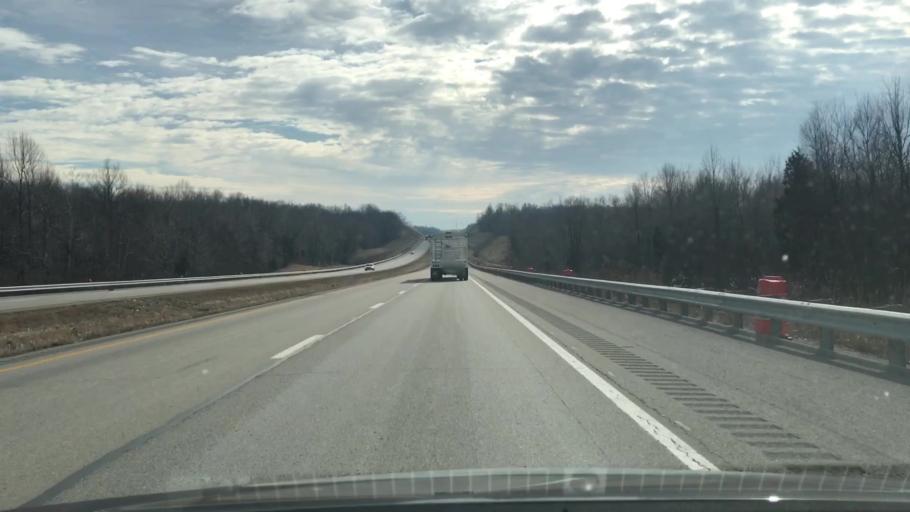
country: US
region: Kentucky
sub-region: Daviess County
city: Masonville
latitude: 37.5759
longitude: -86.9541
